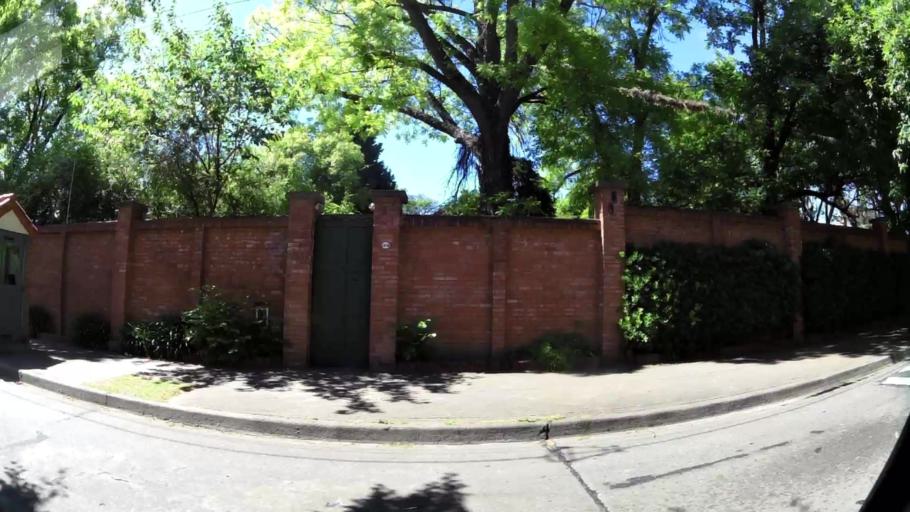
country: AR
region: Buenos Aires
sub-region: Partido de Vicente Lopez
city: Olivos
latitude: -34.5153
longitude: -58.4868
